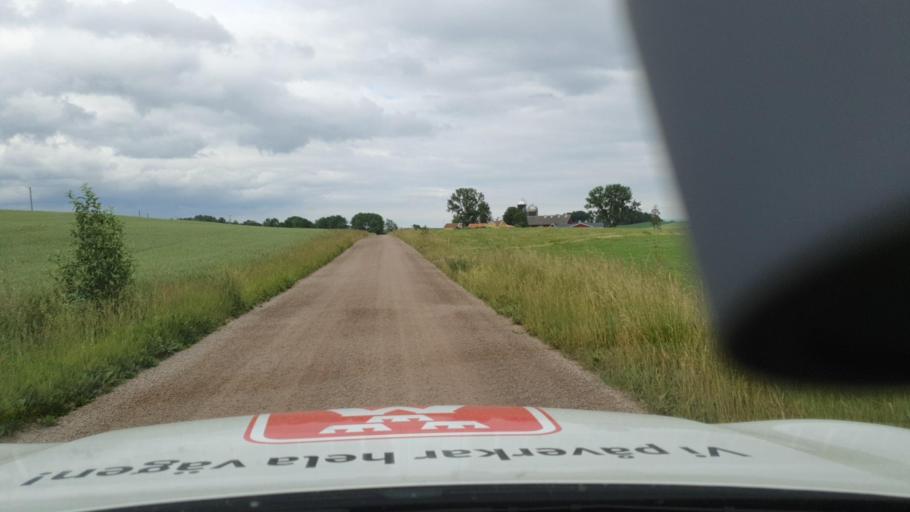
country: SE
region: Vaestra Goetaland
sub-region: Hjo Kommun
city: Hjo
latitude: 58.2103
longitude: 14.1855
